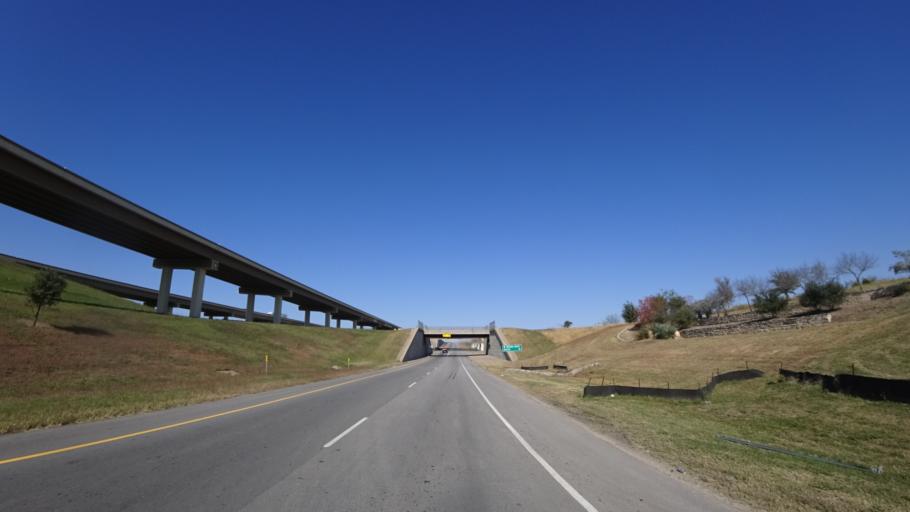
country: US
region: Texas
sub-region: Williamson County
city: Hutto
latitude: 30.5366
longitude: -97.5755
